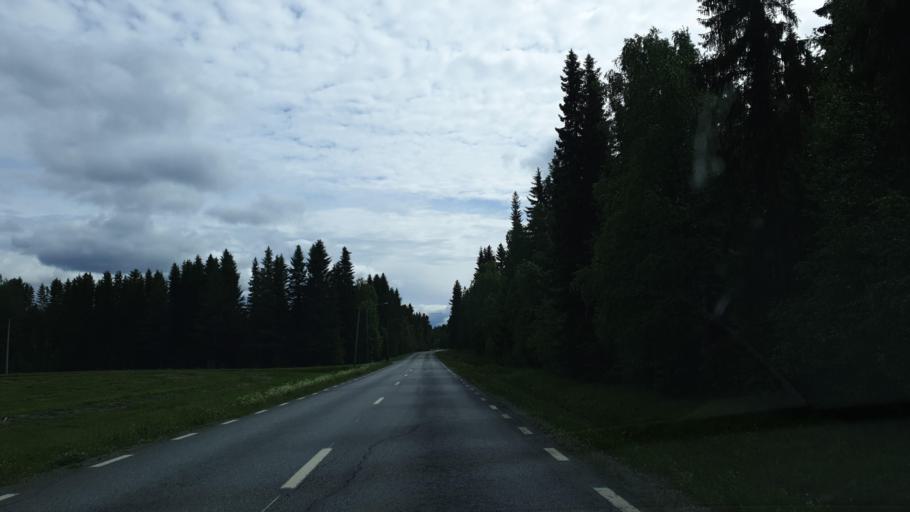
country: SE
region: Vaesterbotten
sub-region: Vilhelmina Kommun
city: Sjoberg
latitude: 64.6705
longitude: 16.2973
